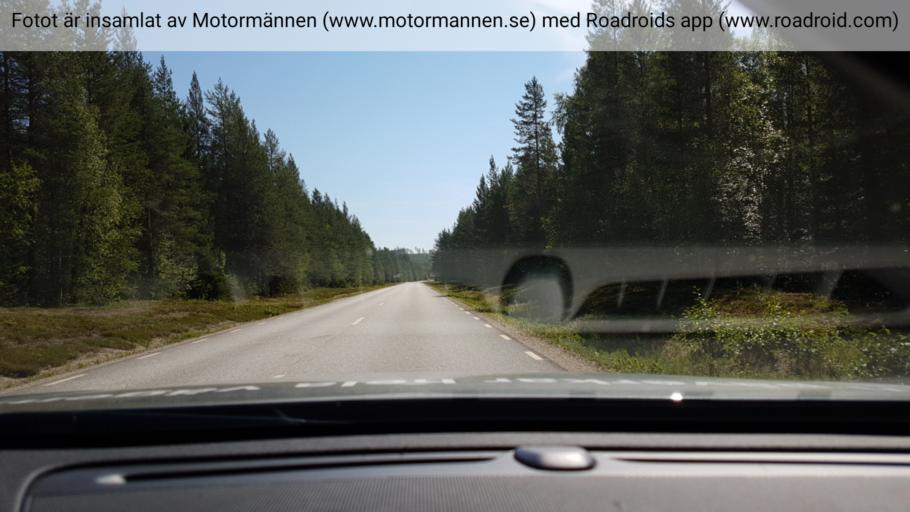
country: SE
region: Vaesterbotten
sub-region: Vindelns Kommun
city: Vindeln
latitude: 64.3638
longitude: 19.4402
